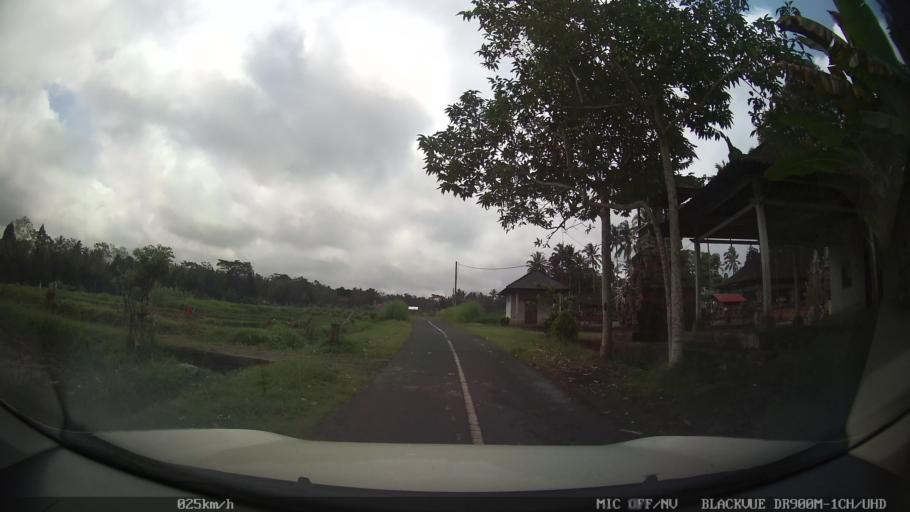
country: ID
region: Bali
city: Bunutan
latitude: -8.4671
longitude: 115.2349
